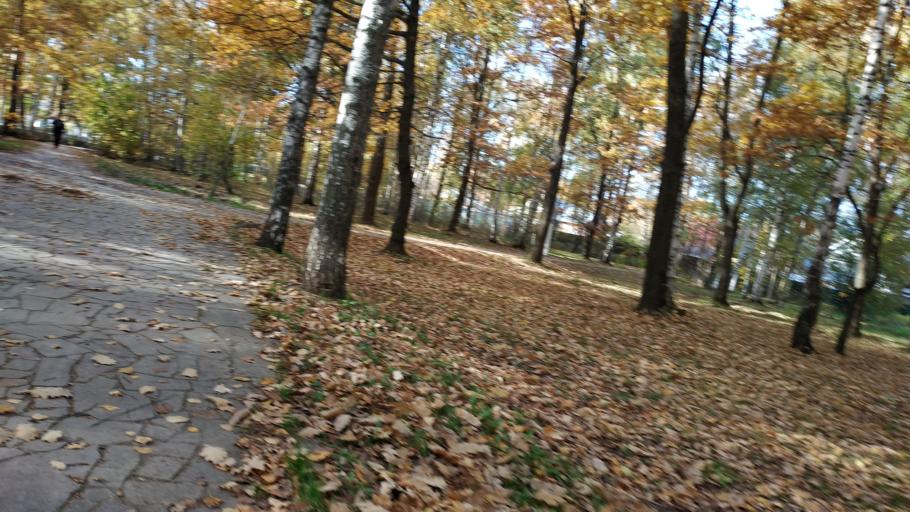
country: RU
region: Moskovskaya
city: Sheremet'yevskiy
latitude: 55.9843
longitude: 37.4904
